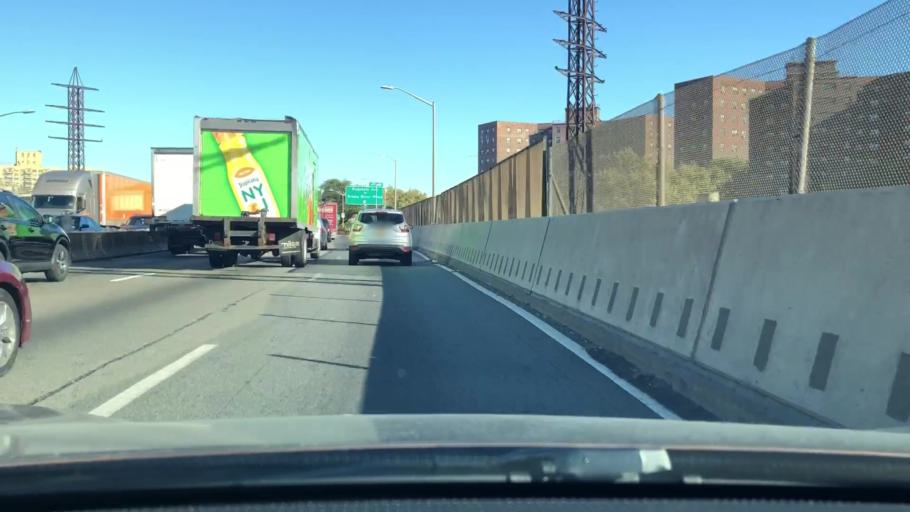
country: US
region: New York
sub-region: Bronx
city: The Bronx
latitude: 40.8366
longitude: -73.8781
